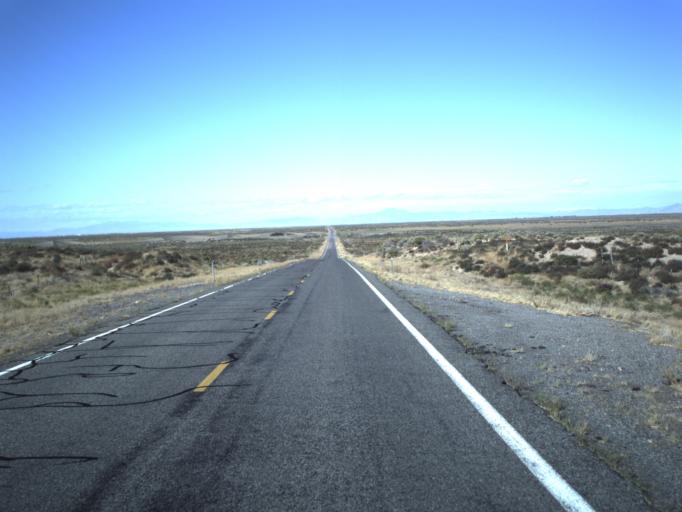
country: US
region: Utah
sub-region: Millard County
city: Delta
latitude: 39.3548
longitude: -112.3849
